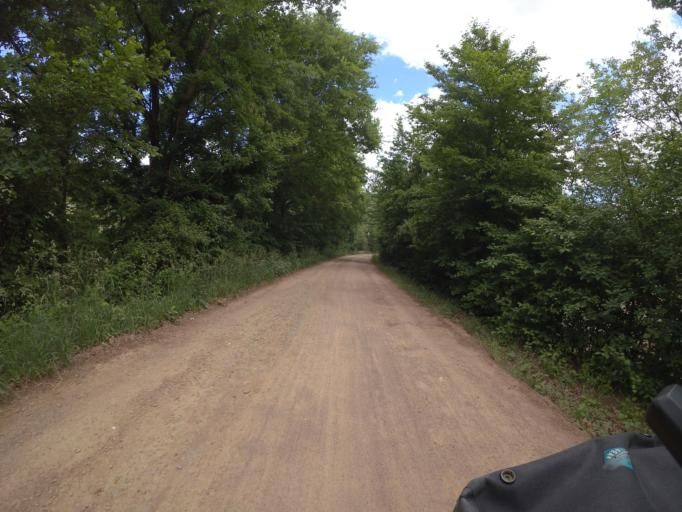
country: DE
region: Rheinland-Pfalz
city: Traisen
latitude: 49.8126
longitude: 7.8234
